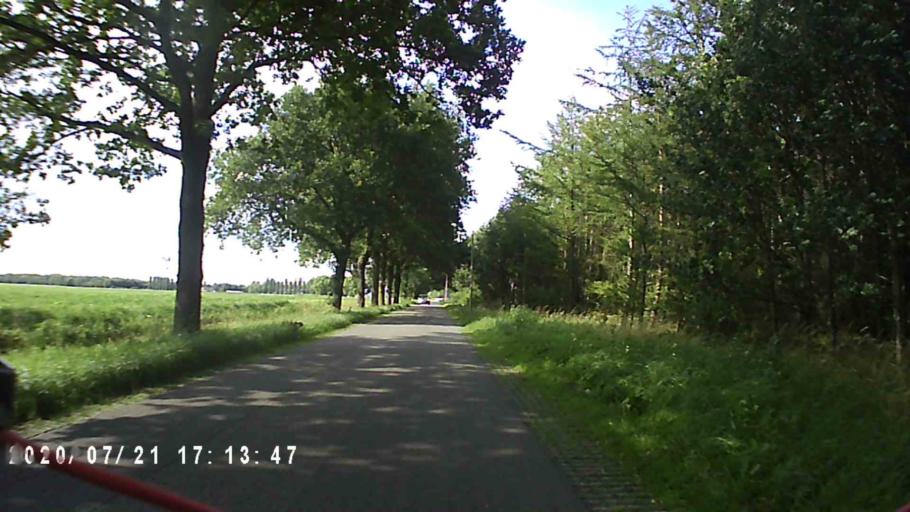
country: NL
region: Groningen
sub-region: Gemeente Hoogezand-Sappemeer
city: Hoogezand
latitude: 53.1393
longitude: 6.7577
